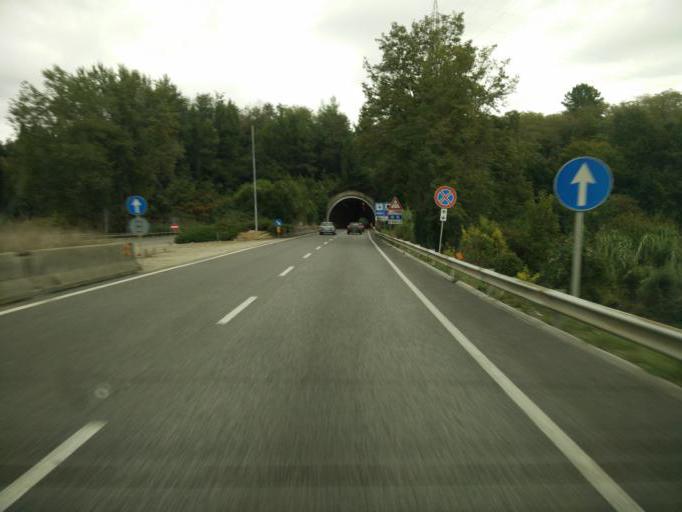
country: IT
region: Tuscany
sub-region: Provincia di Siena
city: Belverde
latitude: 43.3421
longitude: 11.2958
